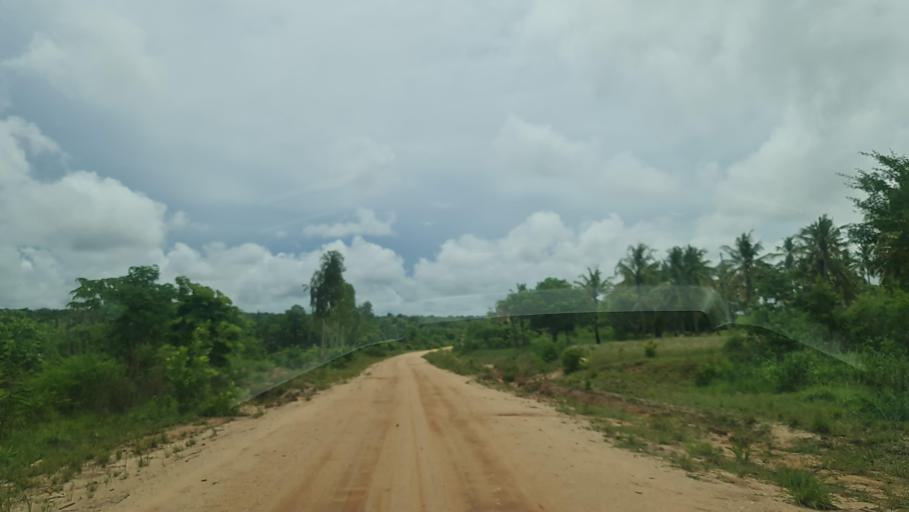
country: MZ
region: Zambezia
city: Quelimane
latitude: -17.2681
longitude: 37.2500
